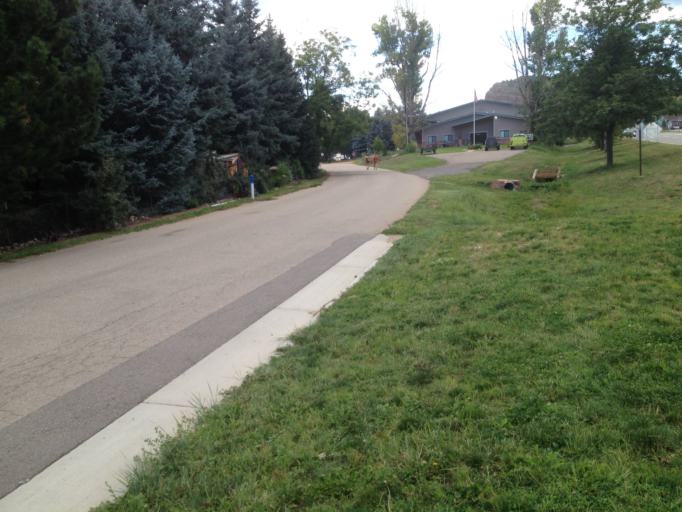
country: US
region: Colorado
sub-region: Boulder County
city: Lyons
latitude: 40.2228
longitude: -105.2657
